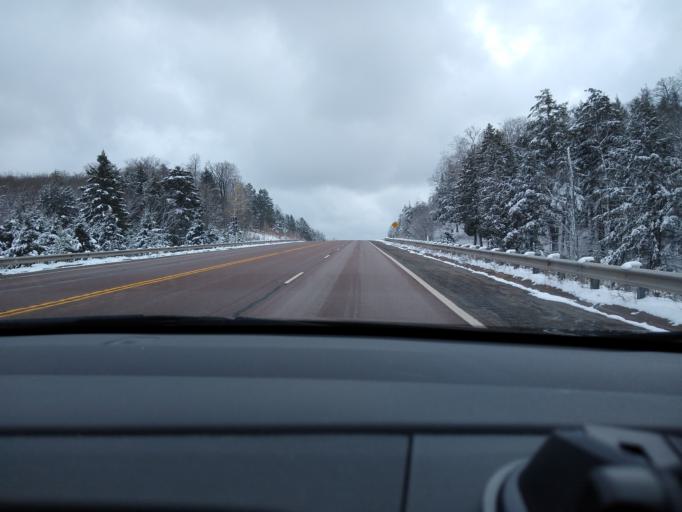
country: US
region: Wisconsin
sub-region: Vilas County
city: Eagle River
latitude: 46.2314
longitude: -89.0791
